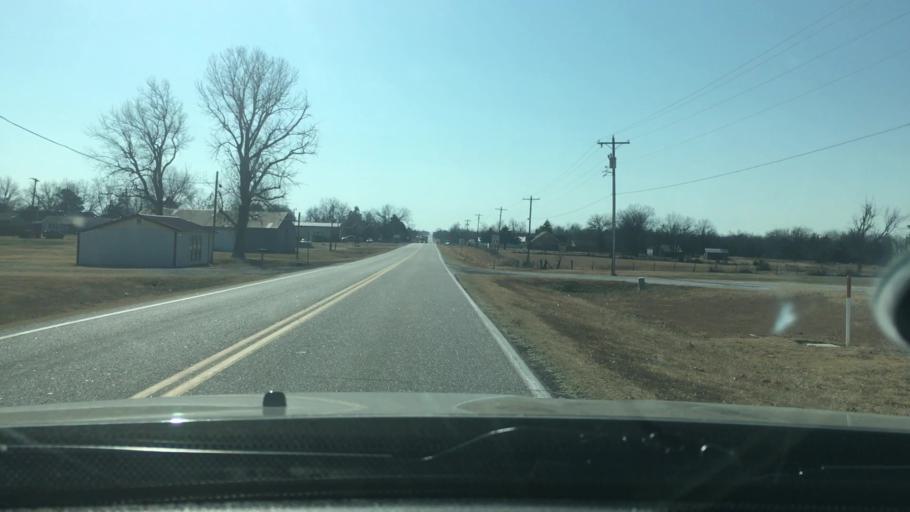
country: US
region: Oklahoma
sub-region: Garvin County
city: Stratford
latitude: 34.8014
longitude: -96.9677
